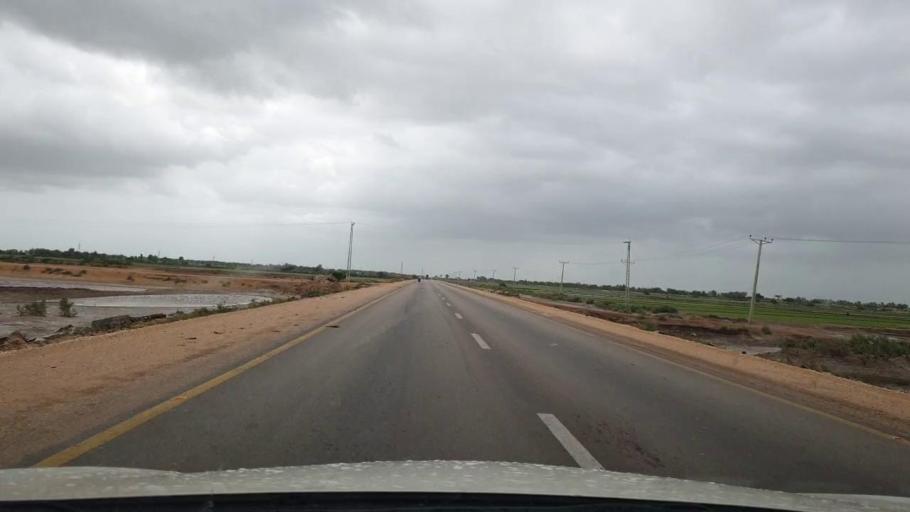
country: PK
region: Sindh
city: Badin
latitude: 24.6559
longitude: 68.7101
